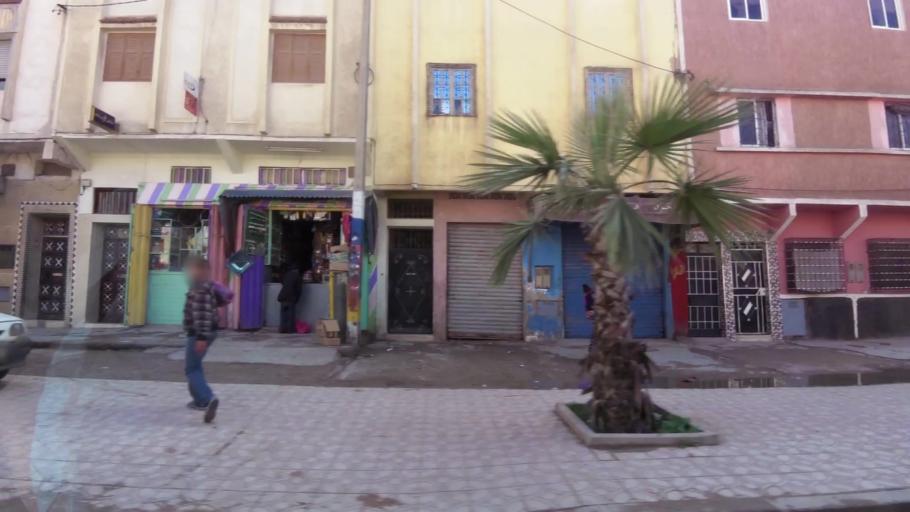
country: MA
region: Chaouia-Ouardigha
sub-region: Settat Province
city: Berrechid
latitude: 33.2729
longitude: -7.5727
